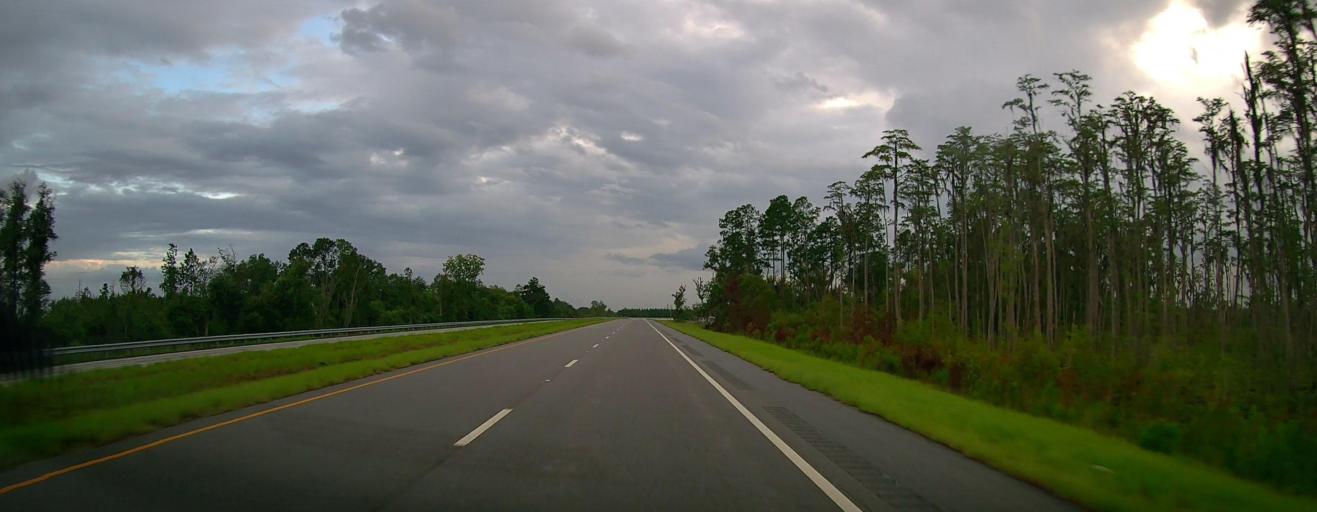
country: US
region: Georgia
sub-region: Ware County
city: Deenwood
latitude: 31.1530
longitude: -82.4404
